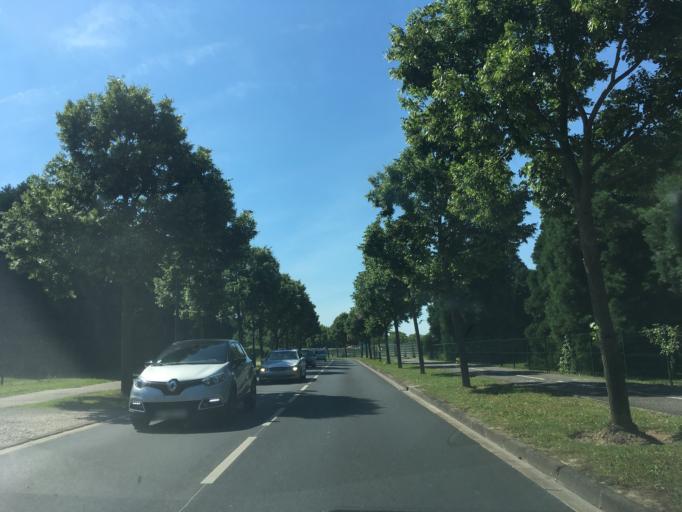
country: FR
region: Ile-de-France
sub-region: Departement de Seine-et-Marne
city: Magny-le-Hongre
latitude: 48.8560
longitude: 2.8151
